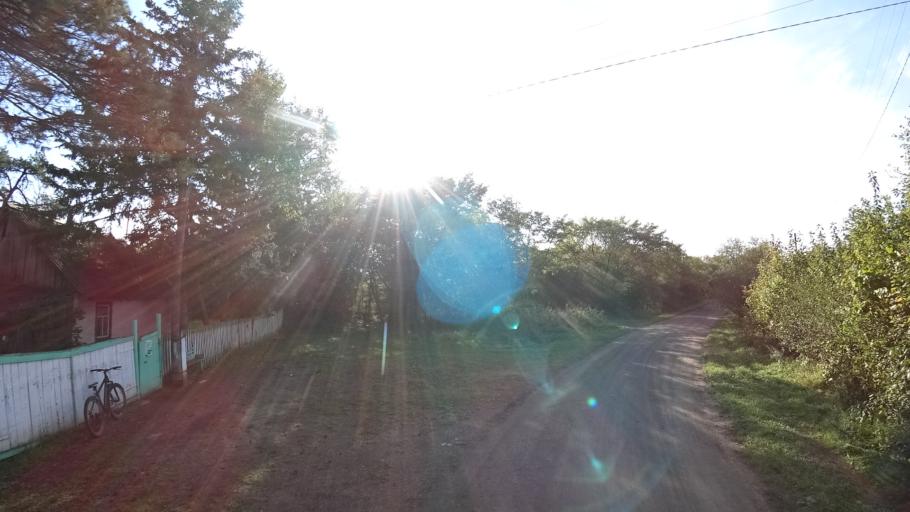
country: RU
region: Amur
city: Arkhara
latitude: 49.3508
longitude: 130.1130
